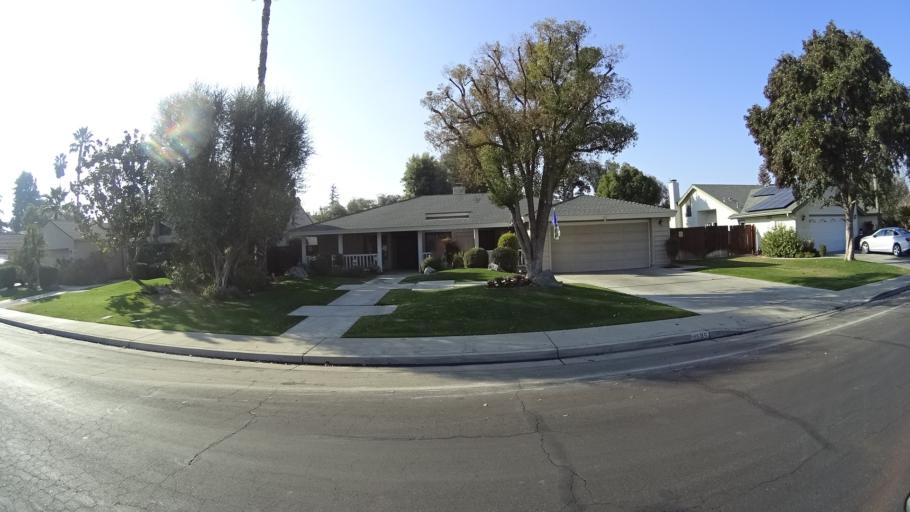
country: US
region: California
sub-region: Kern County
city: Greenacres
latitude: 35.3378
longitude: -119.1092
